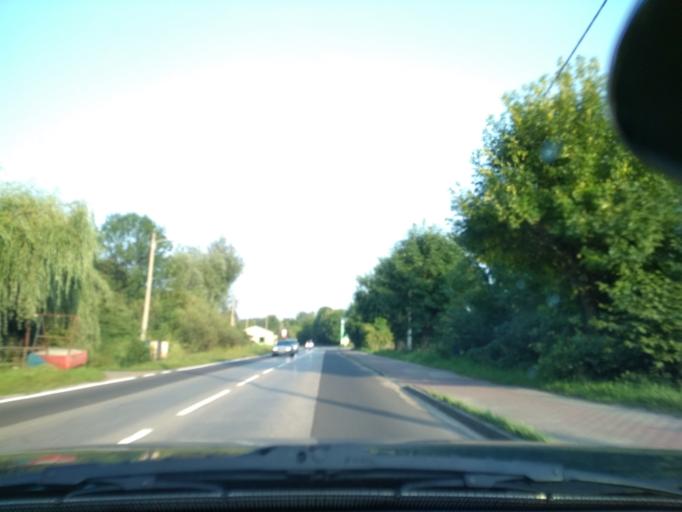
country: PL
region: Silesian Voivodeship
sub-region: Powiat zawiercianski
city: Ogrodzieniec
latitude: 50.4561
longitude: 19.5031
